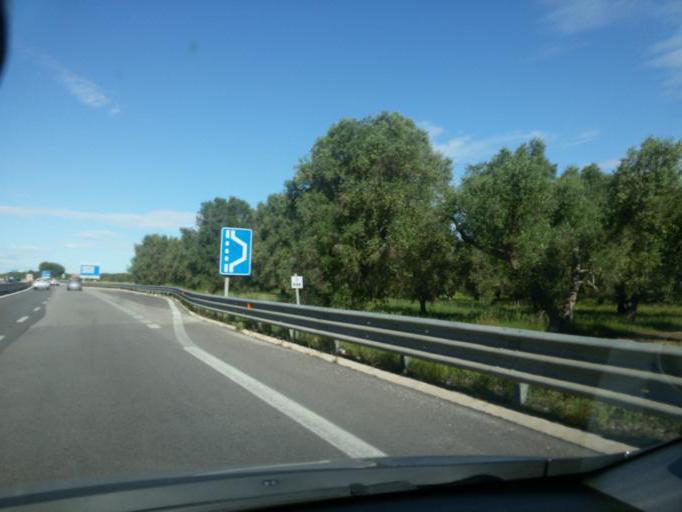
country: IT
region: Apulia
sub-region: Provincia di Brindisi
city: Latiano
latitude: 40.5641
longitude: 17.7444
